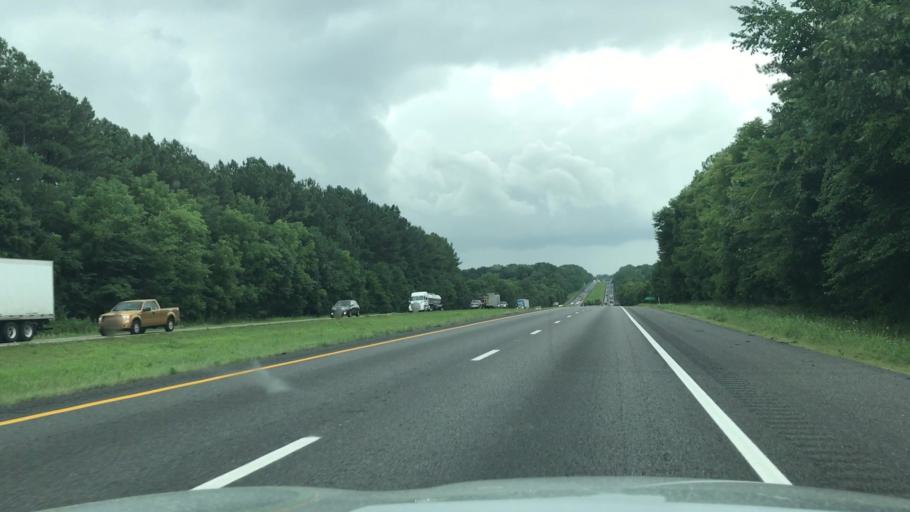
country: US
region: Tennessee
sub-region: Sumner County
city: White House
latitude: 36.5156
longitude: -86.6511
